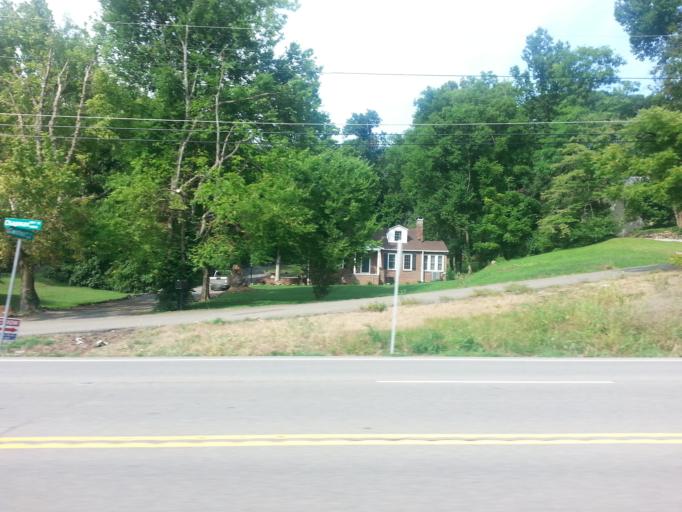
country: US
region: Tennessee
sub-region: Knox County
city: Knoxville
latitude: 35.9303
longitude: -83.9008
